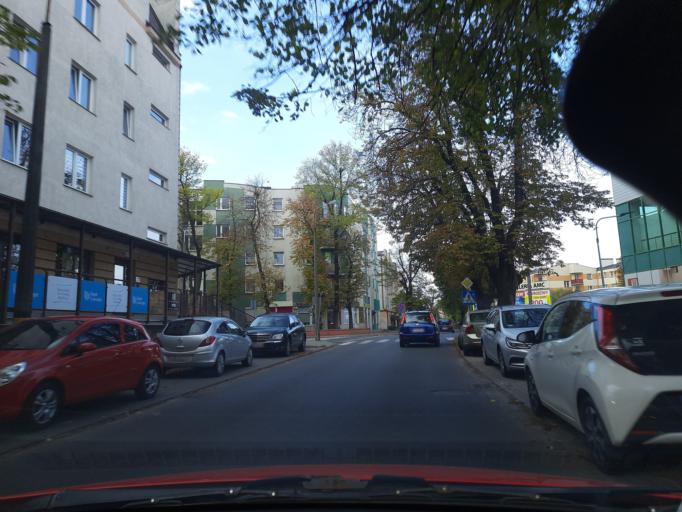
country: PL
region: Kujawsko-Pomorskie
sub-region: Torun
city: Torun
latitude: 53.0240
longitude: 18.6072
